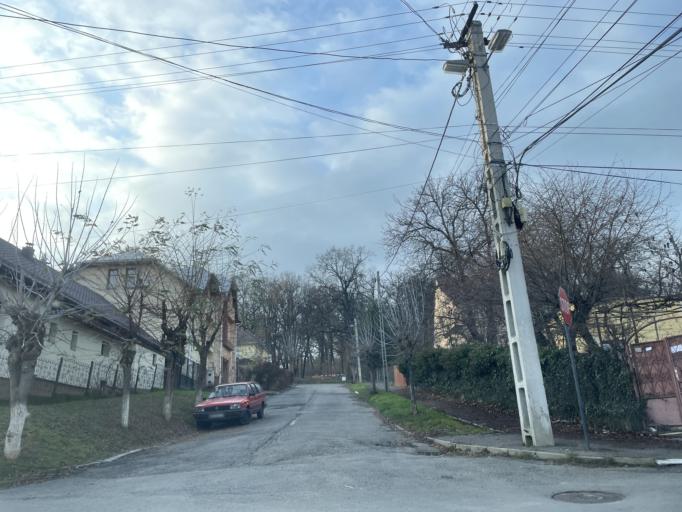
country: RO
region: Mures
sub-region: Municipiul Reghin
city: Reghin
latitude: 46.7821
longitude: 24.6932
